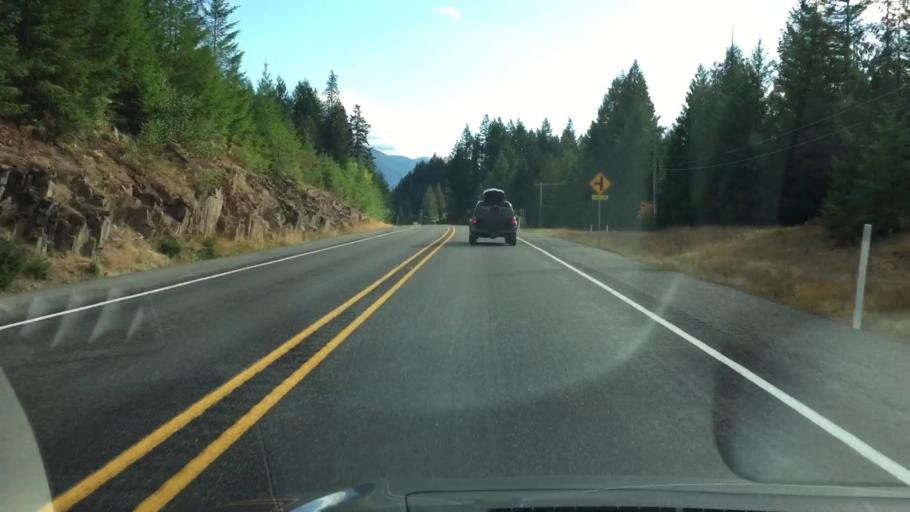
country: US
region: Washington
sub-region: Lewis County
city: Morton
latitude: 46.6206
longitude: -121.6618
